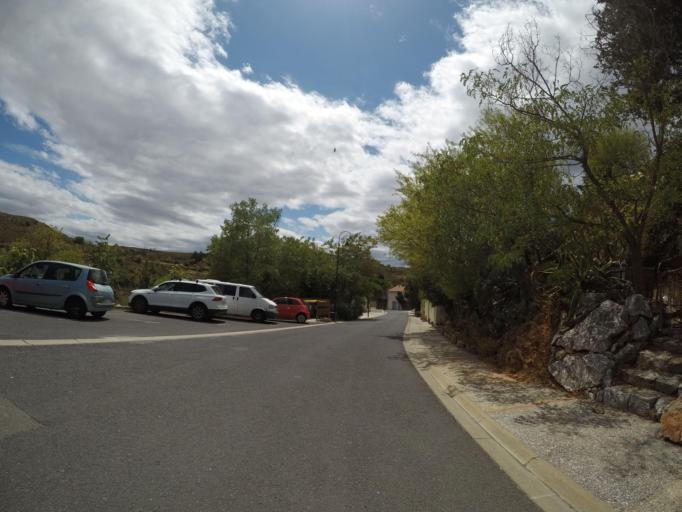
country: FR
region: Languedoc-Roussillon
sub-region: Departement des Pyrenees-Orientales
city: Baixas
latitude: 42.7581
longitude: 2.7552
